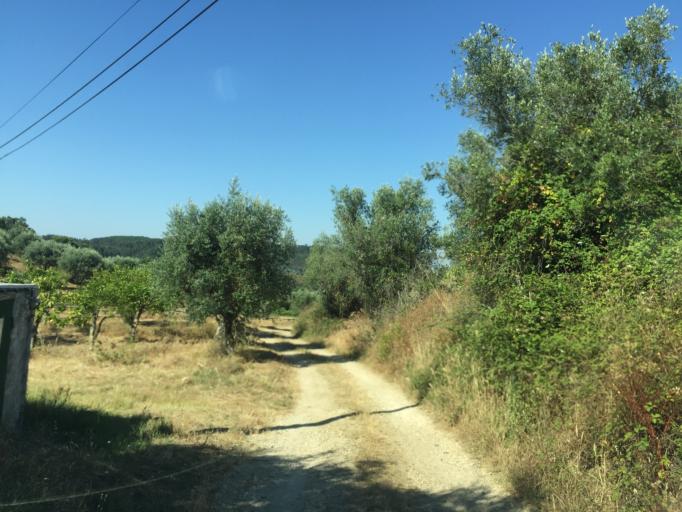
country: PT
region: Santarem
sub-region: Tomar
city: Tomar
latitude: 39.5947
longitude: -8.3257
